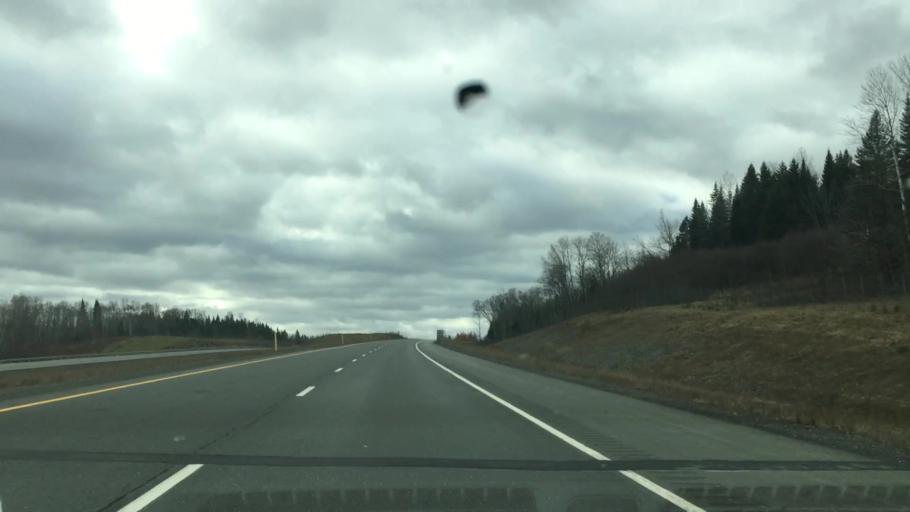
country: US
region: Maine
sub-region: Aroostook County
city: Fort Fairfield
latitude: 46.6619
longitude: -67.7319
